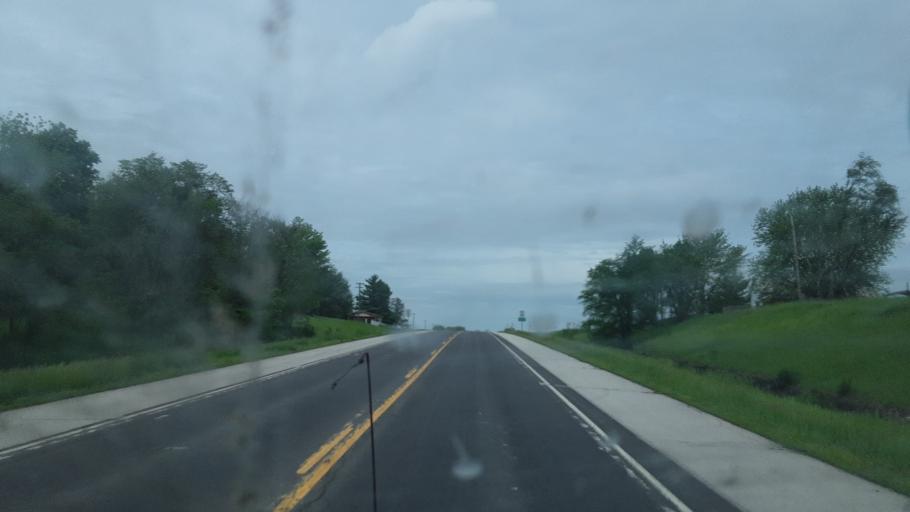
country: US
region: Illinois
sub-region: Hancock County
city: Warsaw
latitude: 40.3945
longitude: -91.5629
